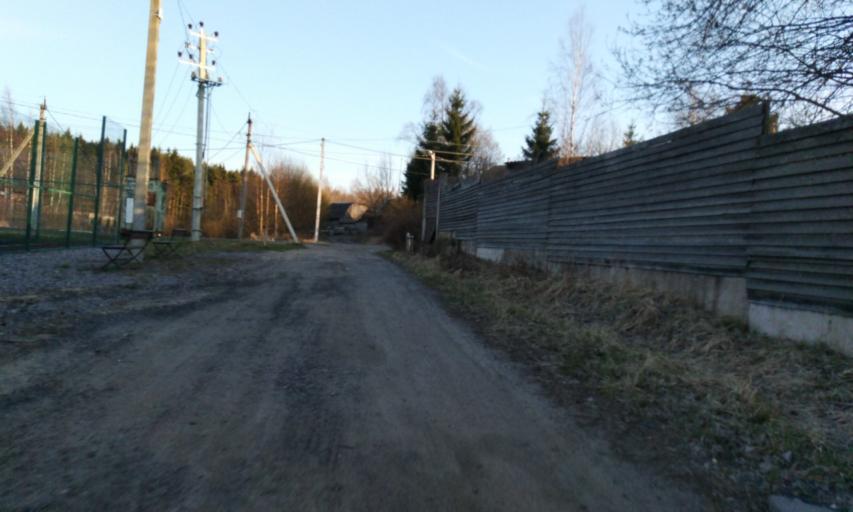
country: RU
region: Leningrad
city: Novoye Devyatkino
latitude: 60.1072
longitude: 30.4543
